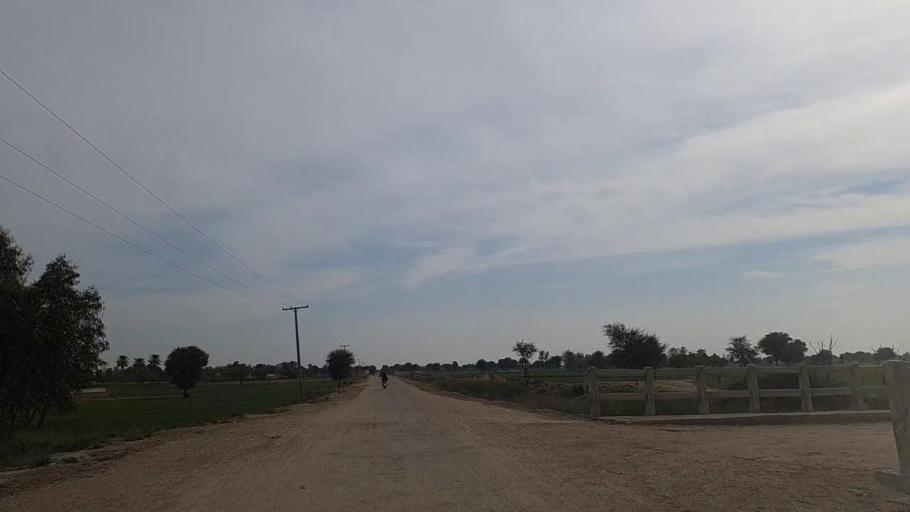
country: PK
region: Sindh
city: Daur
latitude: 26.4224
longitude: 68.4851
